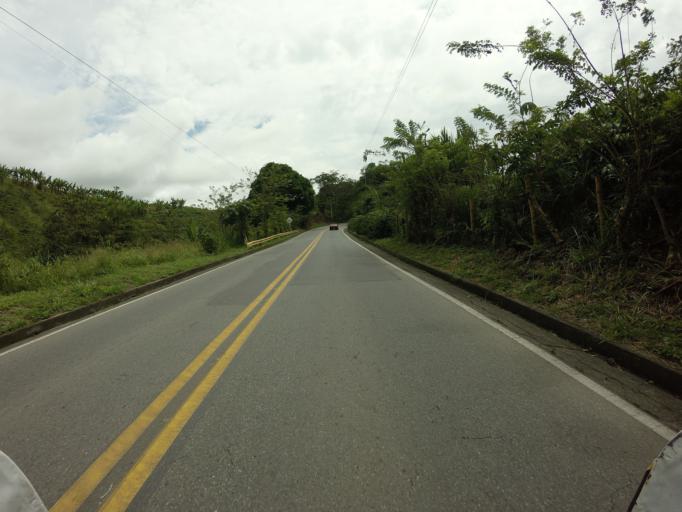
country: CO
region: Quindio
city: Quimbaya
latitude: 4.6014
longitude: -75.7796
